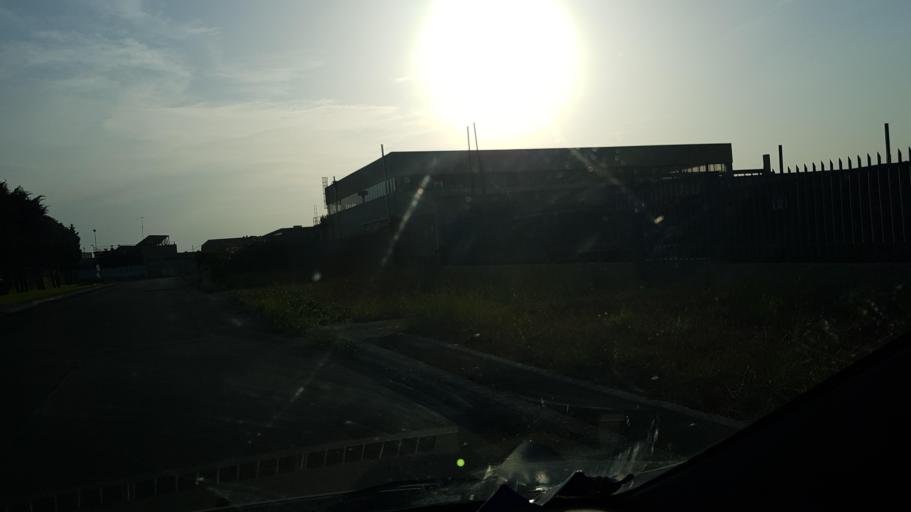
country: IT
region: Apulia
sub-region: Provincia di Brindisi
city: La Rosa
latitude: 40.6280
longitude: 17.9706
